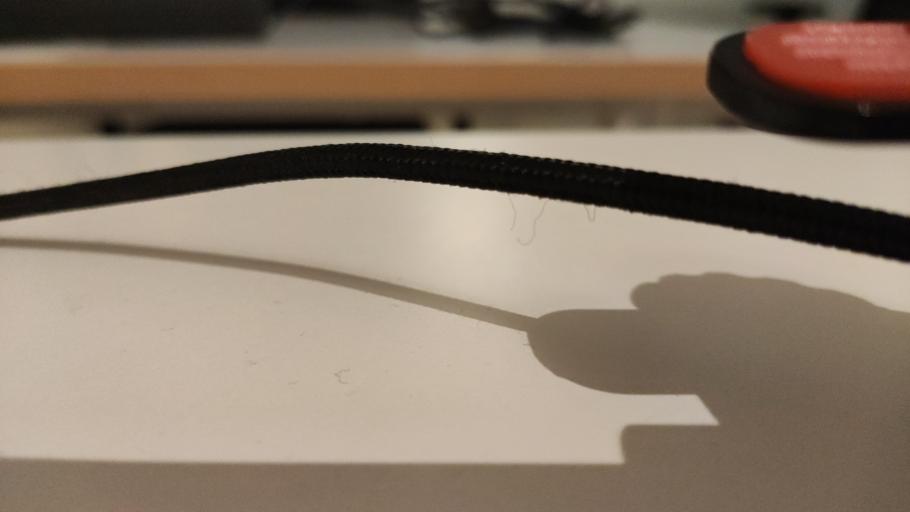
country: RU
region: Moskovskaya
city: Kurovskoye
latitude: 55.6037
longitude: 38.9266
